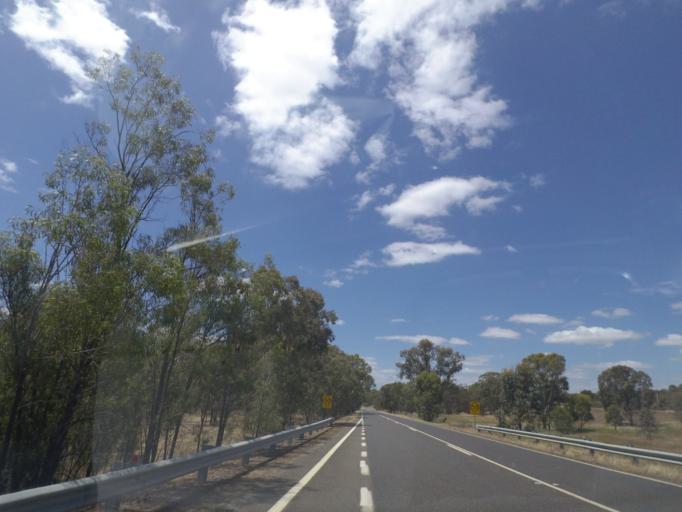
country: AU
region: Victoria
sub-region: Wangaratta
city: Wangaratta
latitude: -36.4659
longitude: 146.2126
